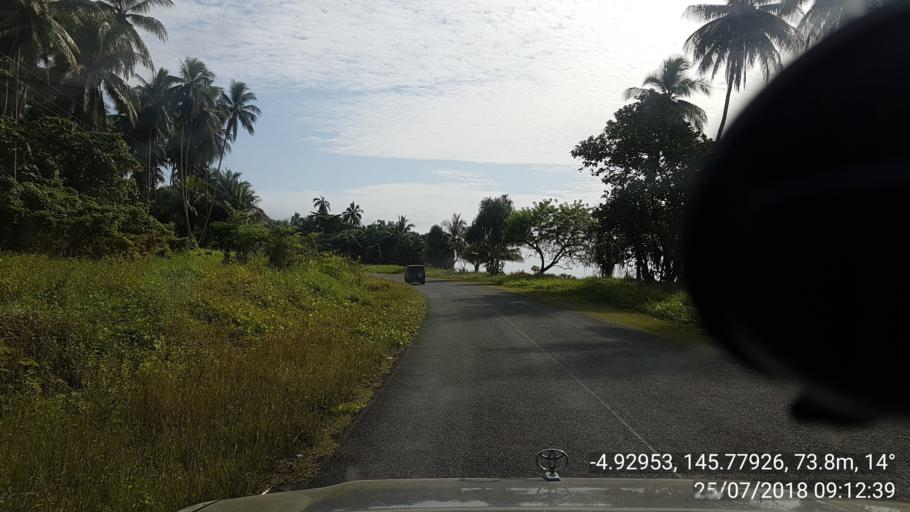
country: PG
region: Madang
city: Madang
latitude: -4.9290
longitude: 145.7796
